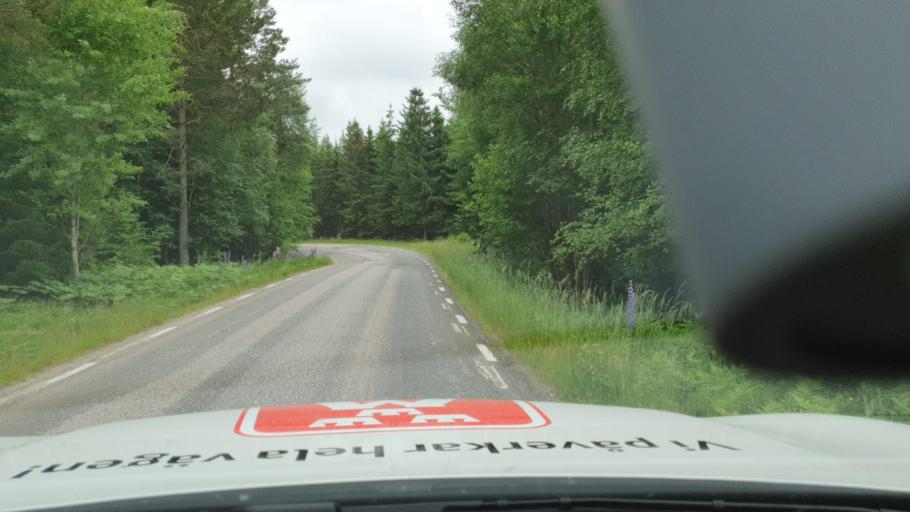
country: SE
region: Vaestra Goetaland
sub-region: Hjo Kommun
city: Hjo
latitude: 58.4057
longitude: 14.2738
